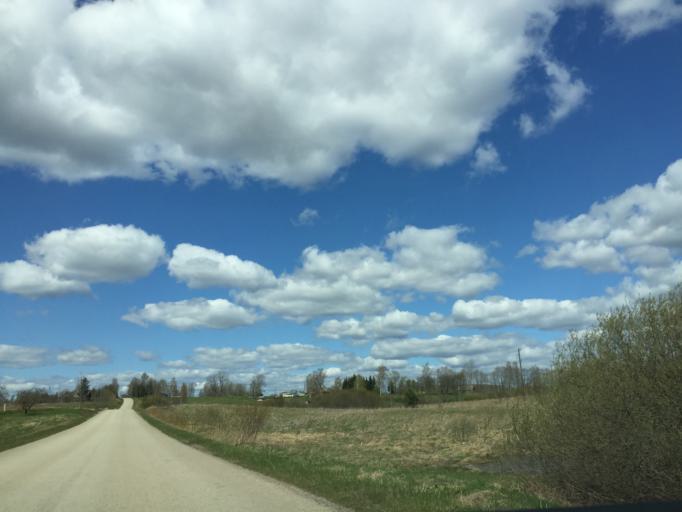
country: LV
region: Rezekne
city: Rezekne
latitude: 56.5543
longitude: 27.1487
